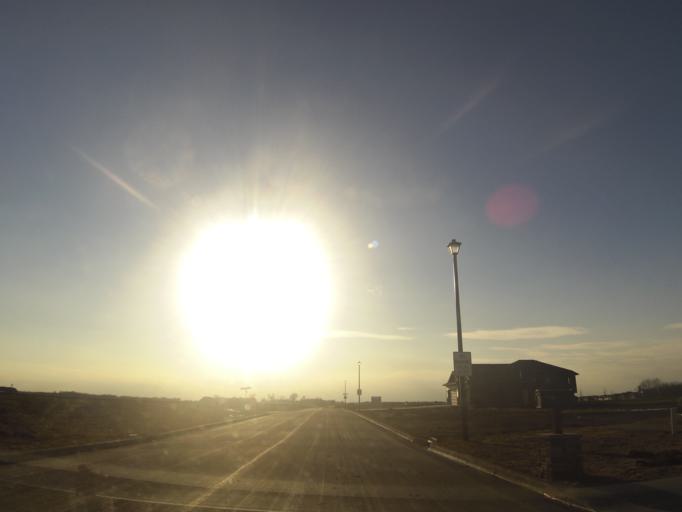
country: US
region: North Dakota
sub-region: Grand Forks County
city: Grand Forks
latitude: 47.8623
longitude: -97.0270
